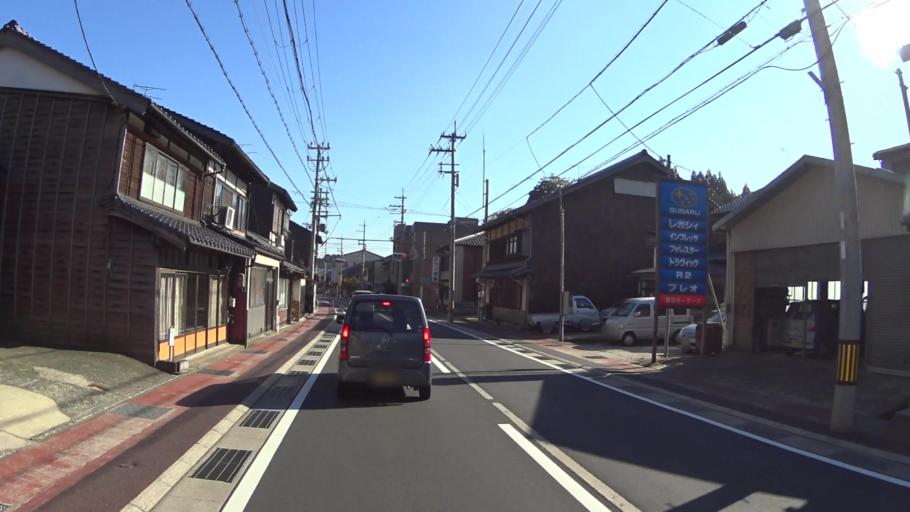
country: JP
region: Kyoto
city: Miyazu
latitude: 35.6274
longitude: 135.0565
